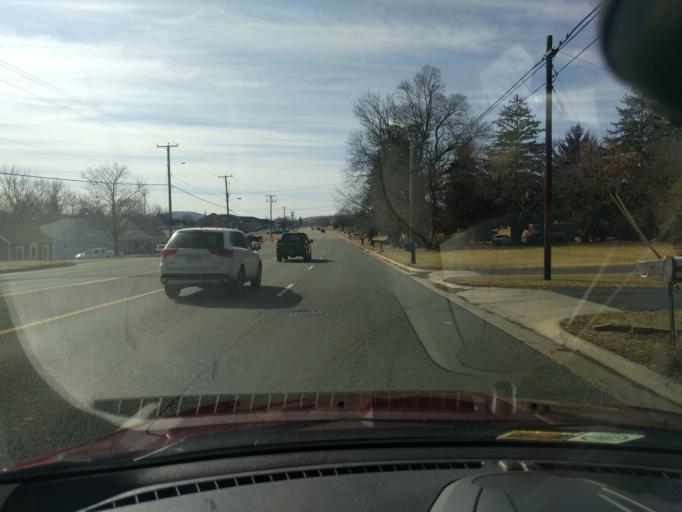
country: US
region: Virginia
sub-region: Augusta County
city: Verona
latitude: 38.1917
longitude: -79.0212
